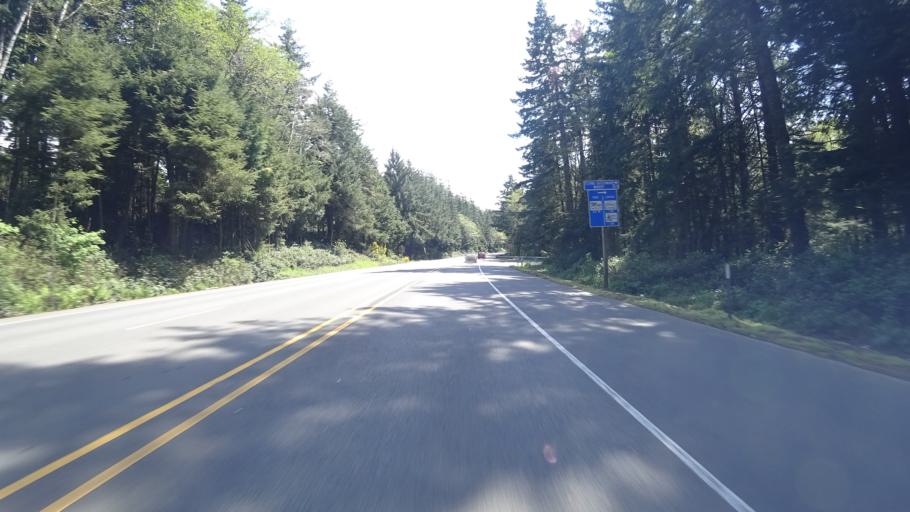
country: US
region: Oregon
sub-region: Lincoln County
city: Depoe Bay
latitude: 44.7496
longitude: -124.0515
